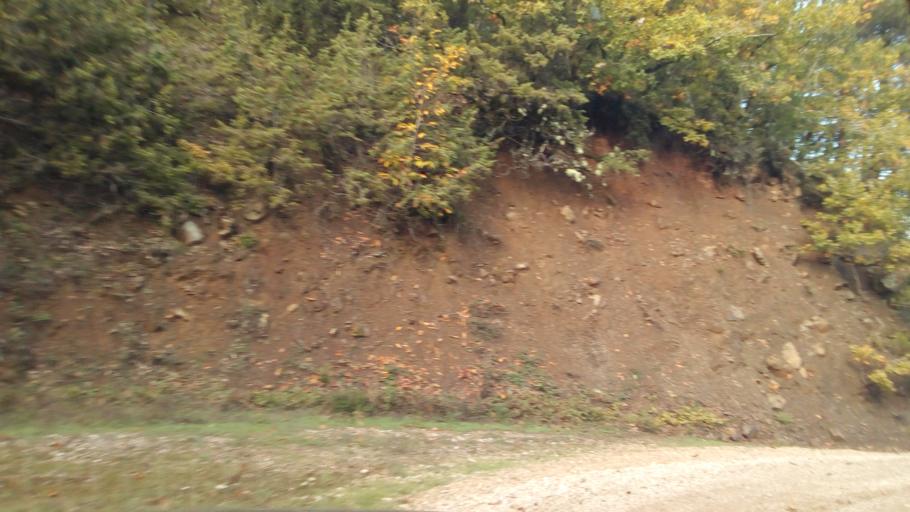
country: GR
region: West Greece
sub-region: Nomos Achaias
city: Kamarai
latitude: 38.4788
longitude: 22.0246
